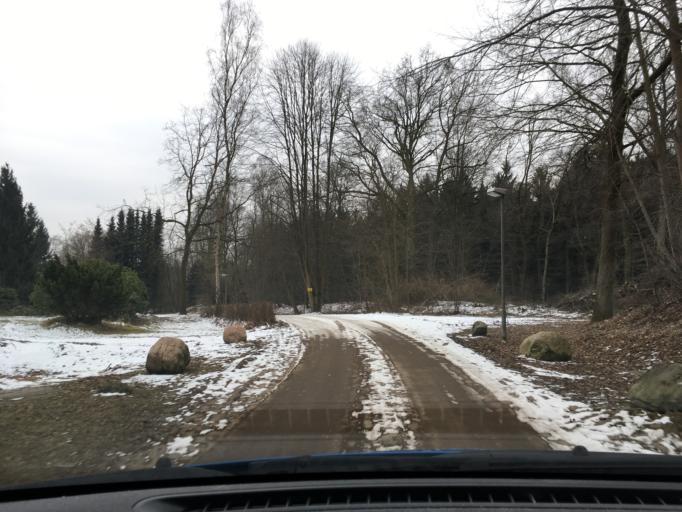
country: DE
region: Lower Saxony
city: Deutsch Evern
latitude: 53.1703
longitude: 10.4280
